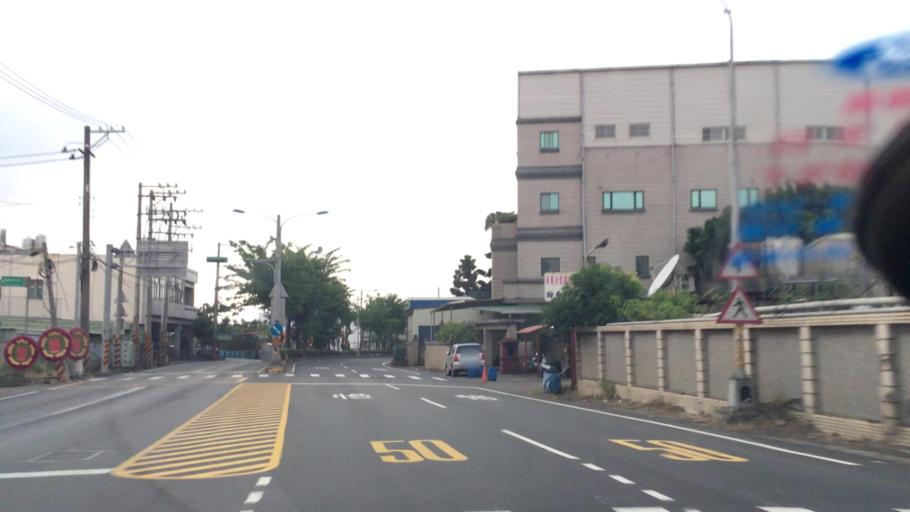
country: TW
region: Taiwan
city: Taoyuan City
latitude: 25.0567
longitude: 121.2686
